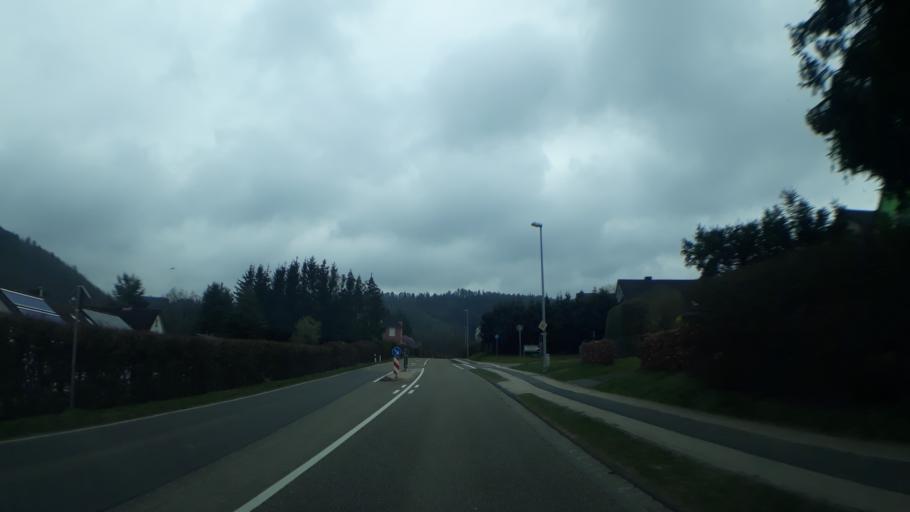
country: DE
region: North Rhine-Westphalia
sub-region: Regierungsbezirk Koln
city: Schleiden
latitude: 50.5395
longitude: 6.4870
